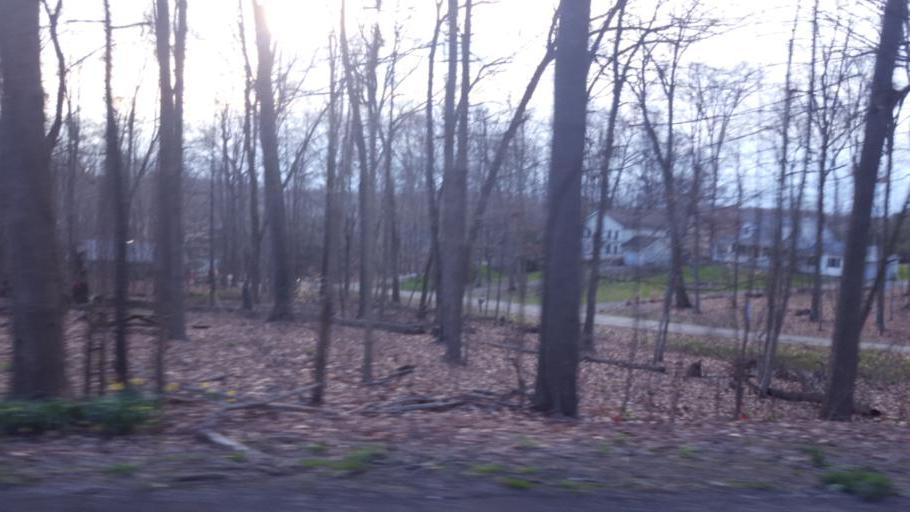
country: US
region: Ohio
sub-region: Knox County
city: Danville
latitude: 40.4419
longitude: -82.3372
